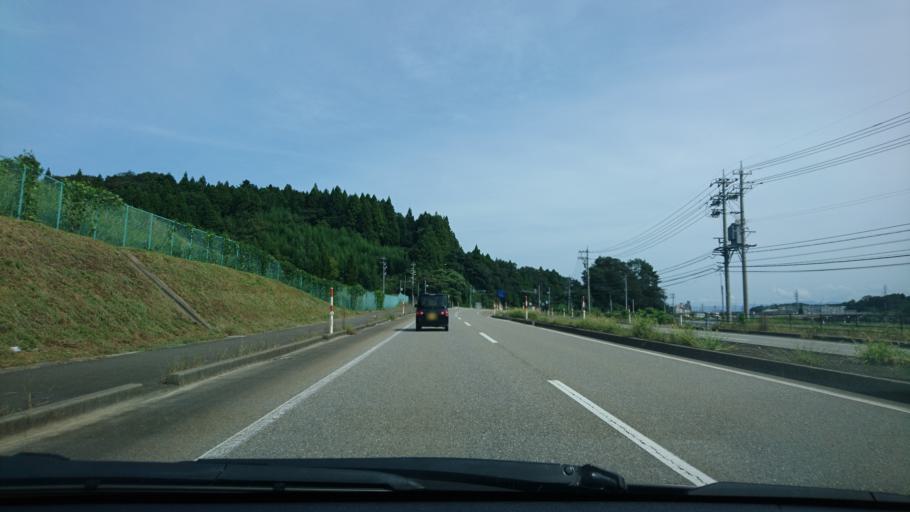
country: JP
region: Fukui
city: Maruoka
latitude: 36.2939
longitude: 136.3010
